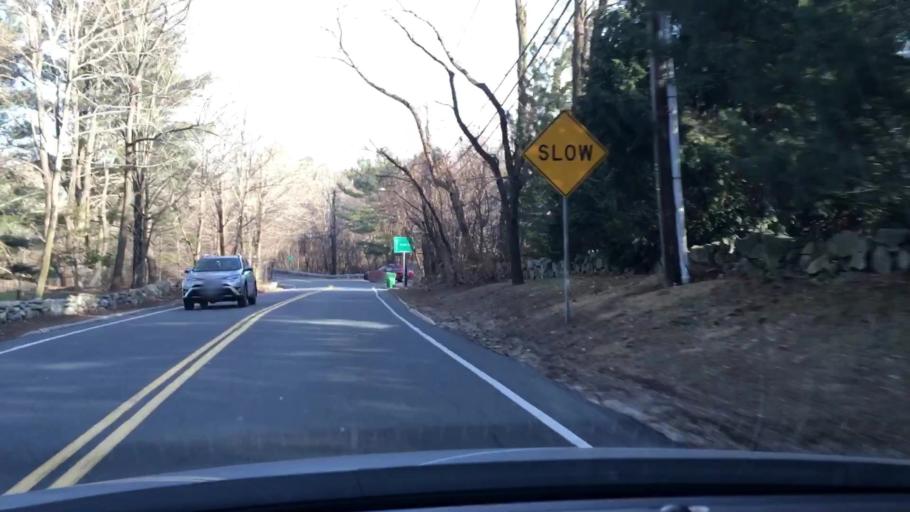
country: US
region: Massachusetts
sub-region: Norfolk County
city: Westwood
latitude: 42.2210
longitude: -71.2037
